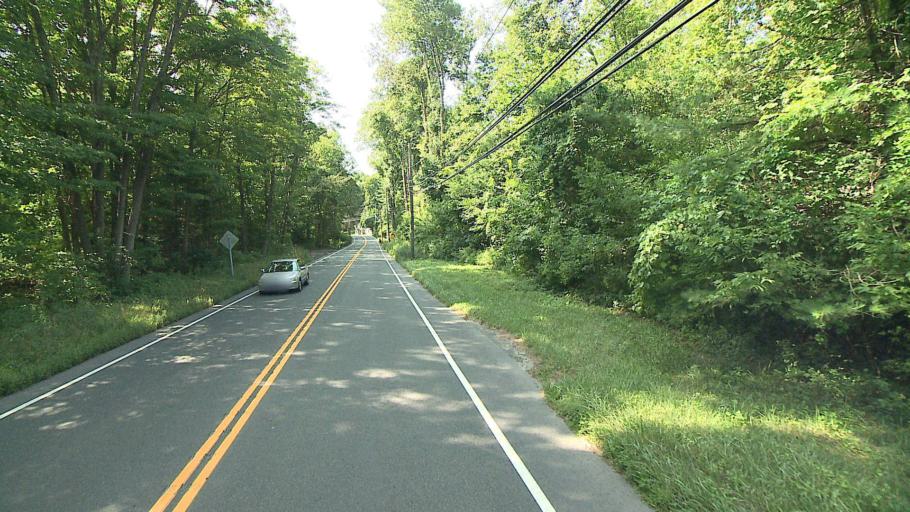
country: US
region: Connecticut
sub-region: Fairfield County
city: Sherman
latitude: 41.5983
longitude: -73.4578
